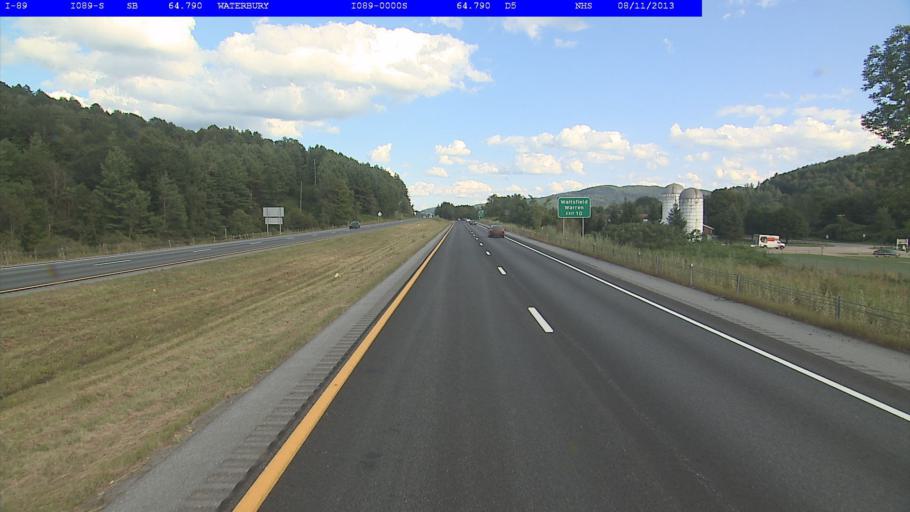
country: US
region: Vermont
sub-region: Washington County
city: Waterbury
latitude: 44.3489
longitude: -72.7706
